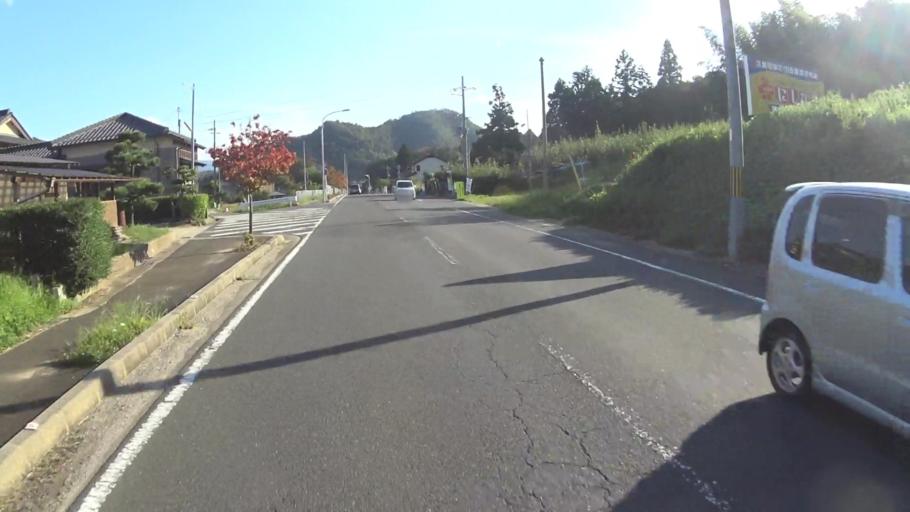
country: JP
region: Hyogo
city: Toyooka
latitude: 35.6146
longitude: 134.9193
